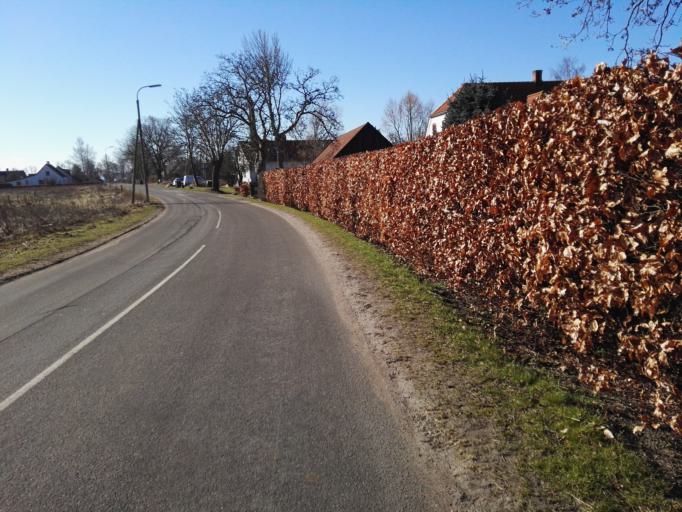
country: DK
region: Zealand
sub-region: Lejre Kommune
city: Ejby
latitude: 55.7616
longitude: 11.8027
